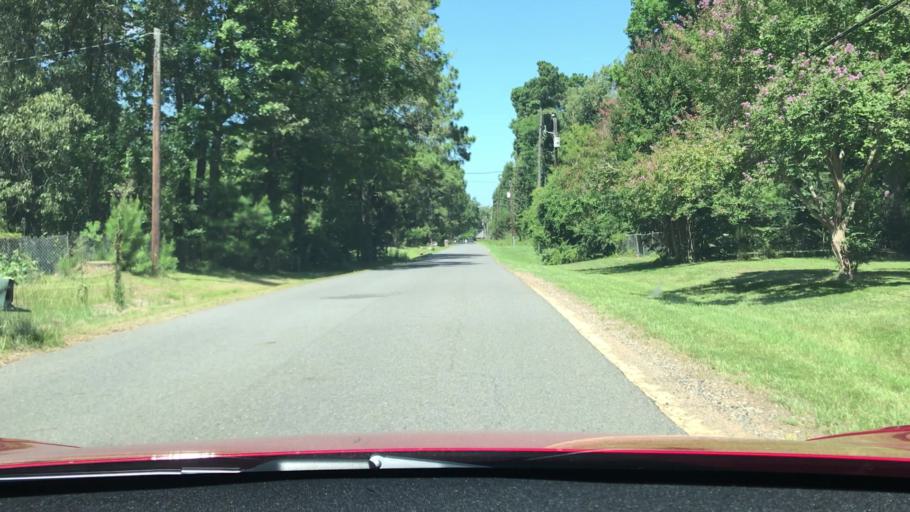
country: US
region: Louisiana
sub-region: De Soto Parish
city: Stonewall
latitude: 32.3448
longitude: -93.7088
